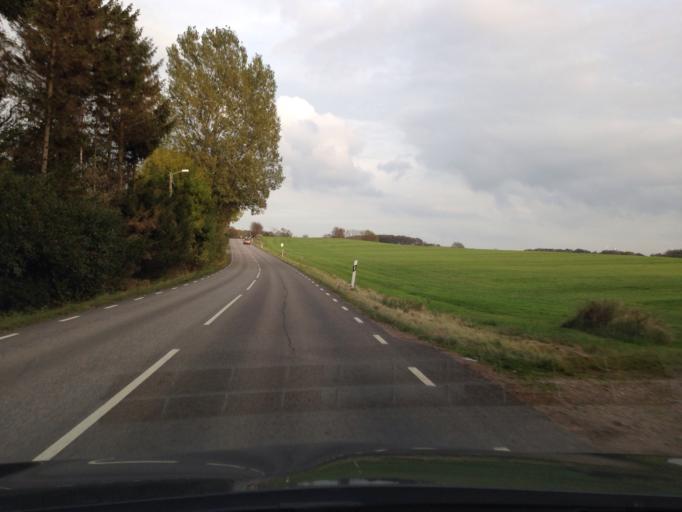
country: SE
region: Skane
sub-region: Bastads Kommun
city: Bastad
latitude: 56.4354
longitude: 12.7386
